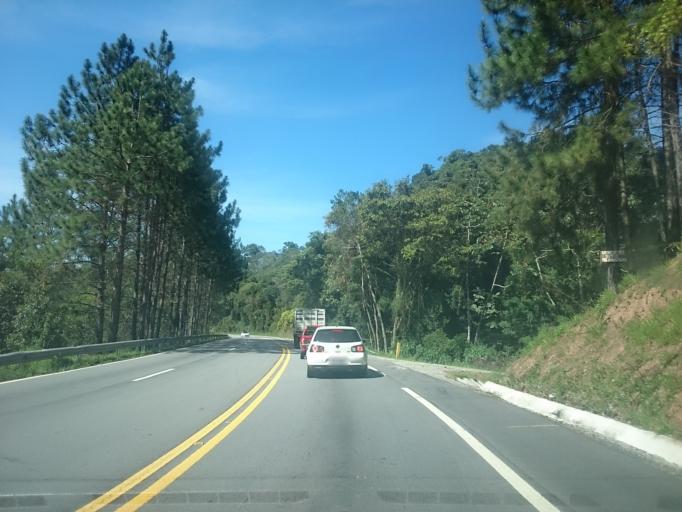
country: BR
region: Santa Catarina
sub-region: Santo Amaro Da Imperatriz
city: Santo Amaro da Imperatriz
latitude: -27.7160
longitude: -48.9432
